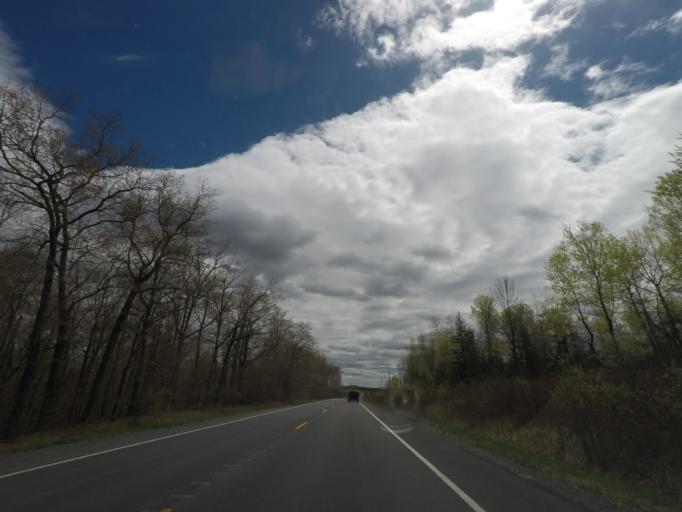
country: US
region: New York
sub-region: Albany County
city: Ravena
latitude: 42.4942
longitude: -73.7941
